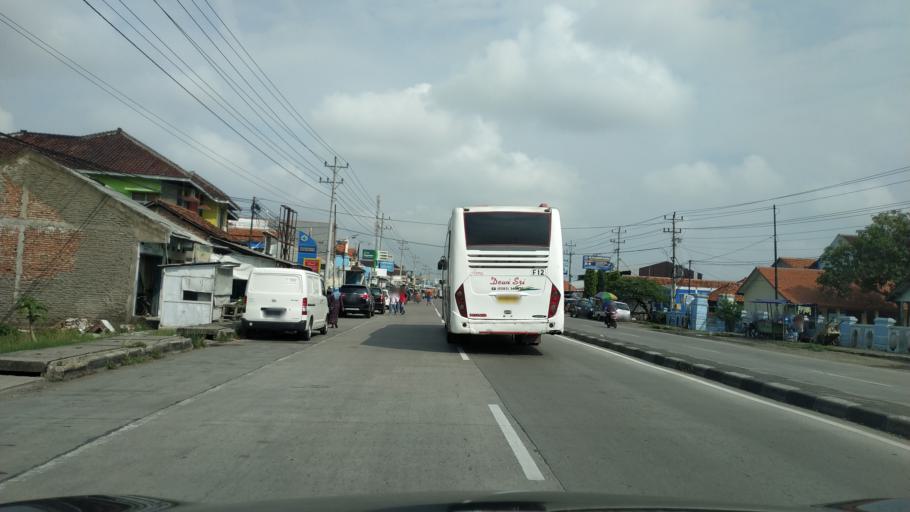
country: ID
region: Central Java
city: Bulakamba
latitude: -6.8745
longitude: 108.9494
